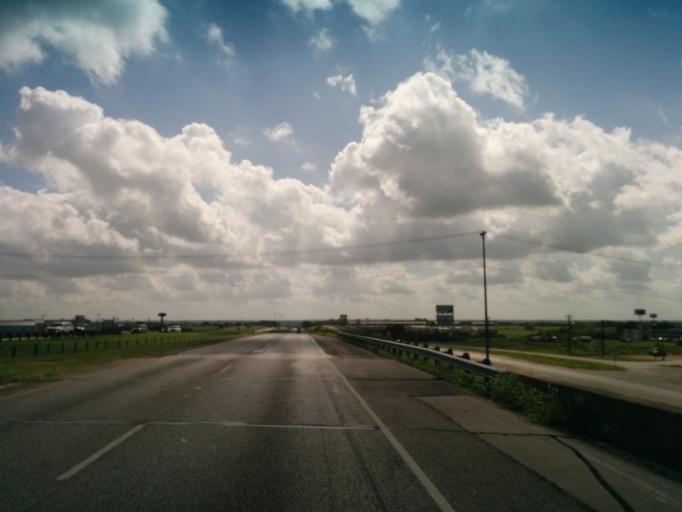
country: US
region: Texas
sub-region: Fayette County
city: Schulenburg
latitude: 29.6933
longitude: -96.9025
